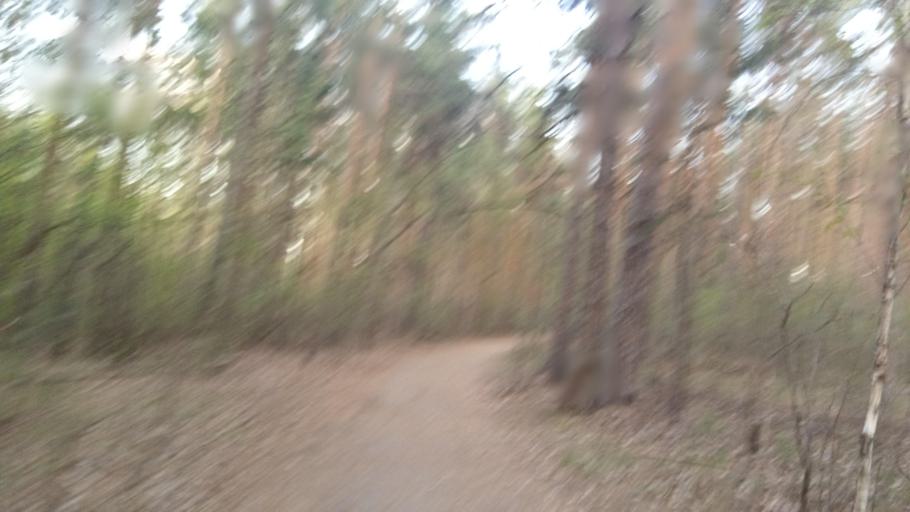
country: RU
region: Chelyabinsk
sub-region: Gorod Chelyabinsk
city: Chelyabinsk
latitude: 55.1667
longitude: 61.3352
